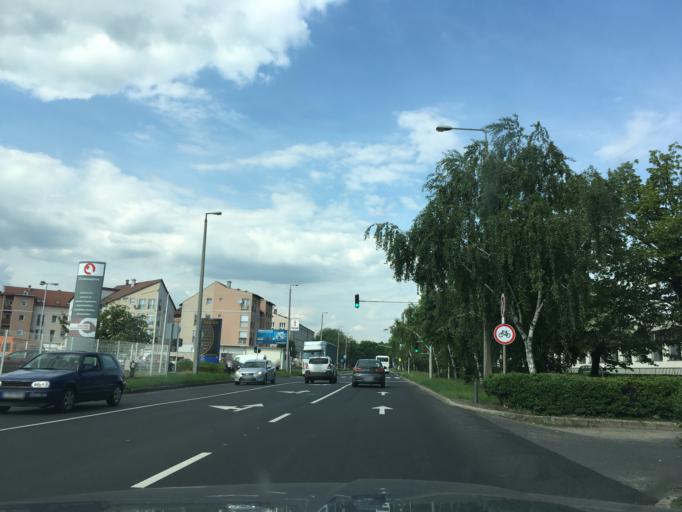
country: HU
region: Hajdu-Bihar
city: Debrecen
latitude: 47.5211
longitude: 21.6167
